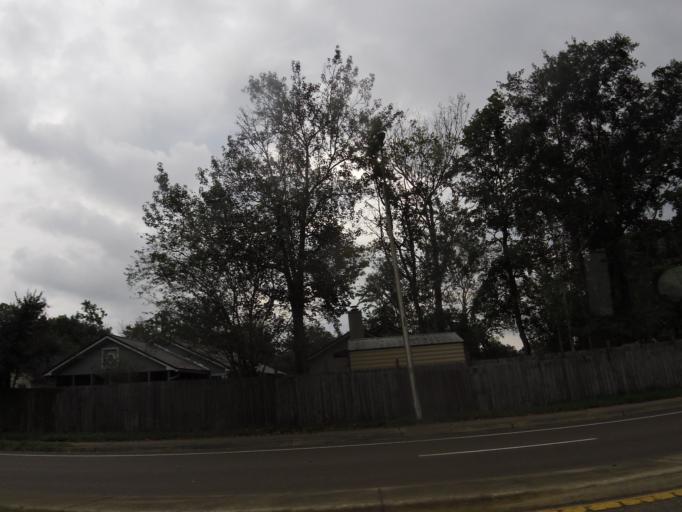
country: US
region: Florida
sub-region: Clay County
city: Bellair-Meadowbrook Terrace
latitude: 30.1972
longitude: -81.7647
